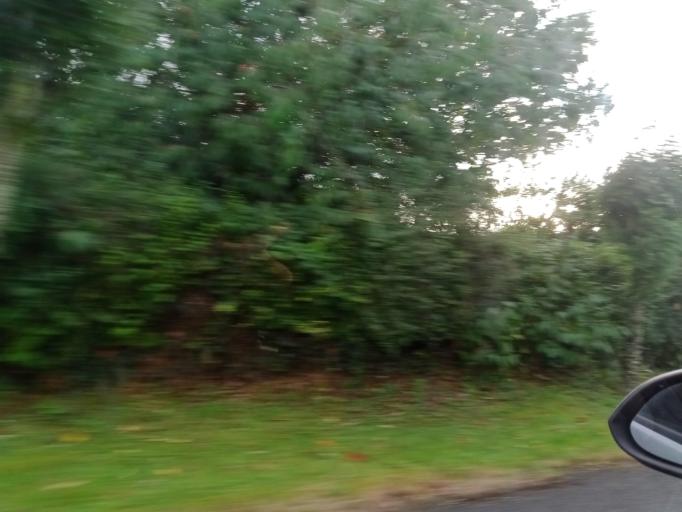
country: IE
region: Leinster
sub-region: Laois
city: Mountmellick
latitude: 53.1362
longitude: -7.4124
